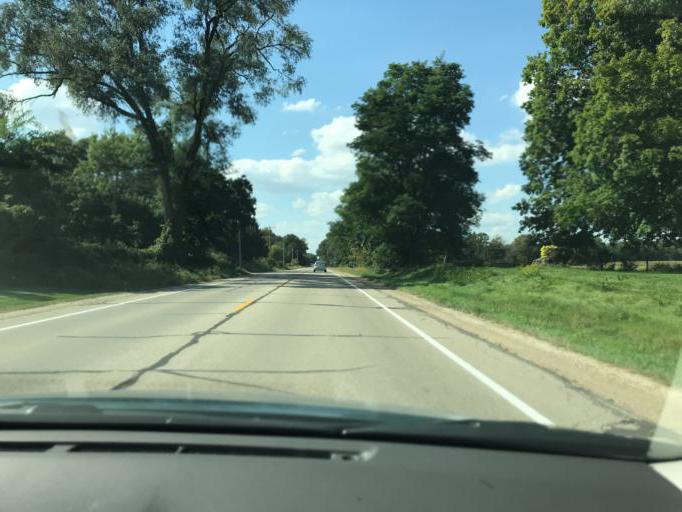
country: US
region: Wisconsin
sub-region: Walworth County
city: Williams Bay
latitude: 42.6057
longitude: -88.5530
